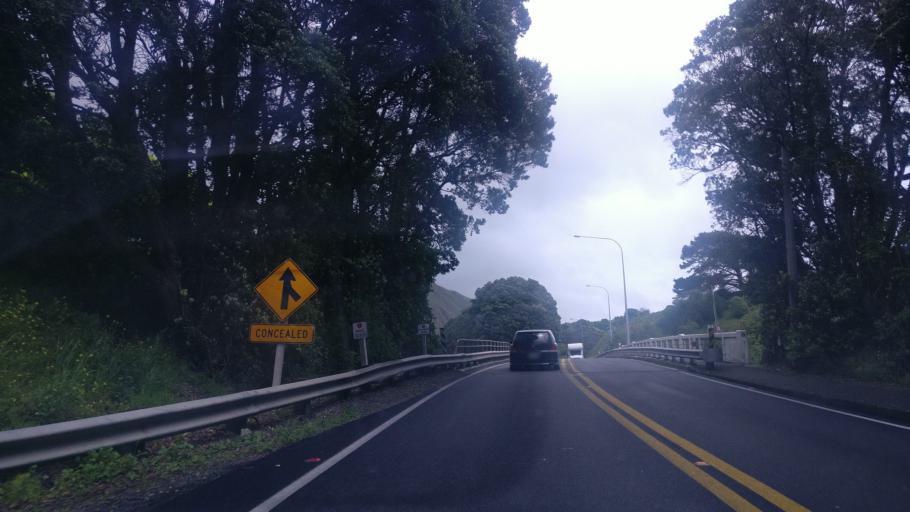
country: NZ
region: Wellington
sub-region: Kapiti Coast District
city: Paraparaumu
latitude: -40.9933
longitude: 174.9474
